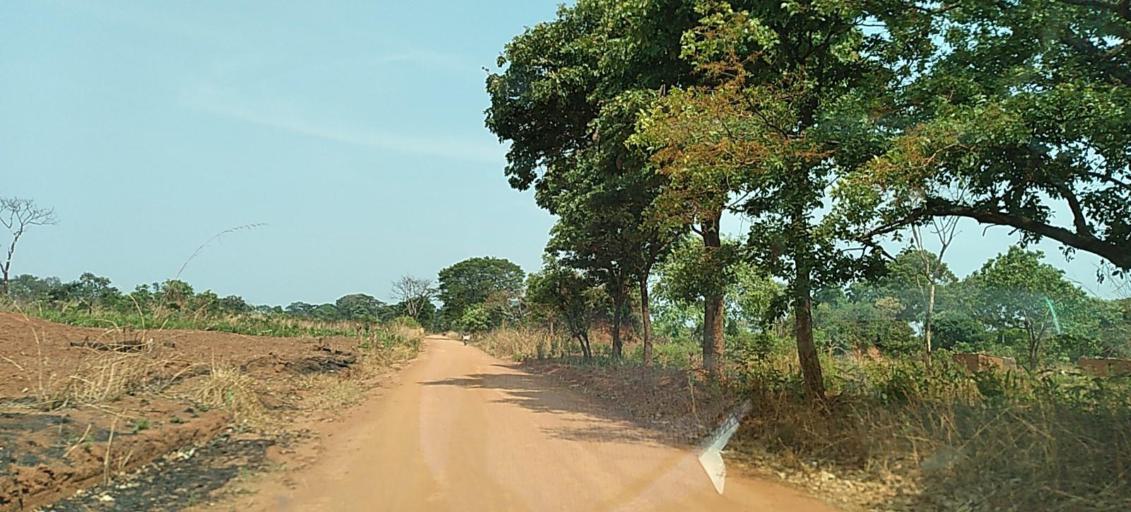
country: ZM
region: Copperbelt
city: Chililabombwe
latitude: -12.3411
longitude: 27.6972
